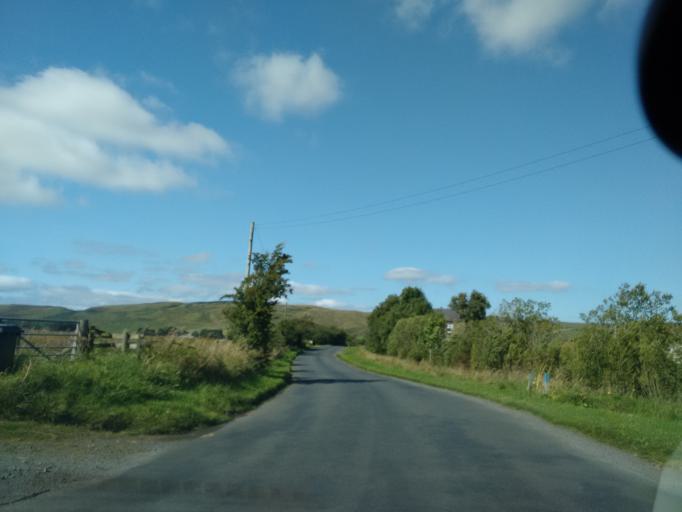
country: GB
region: England
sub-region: Northumberland
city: Bardon Mill
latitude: 54.9899
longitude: -2.3845
